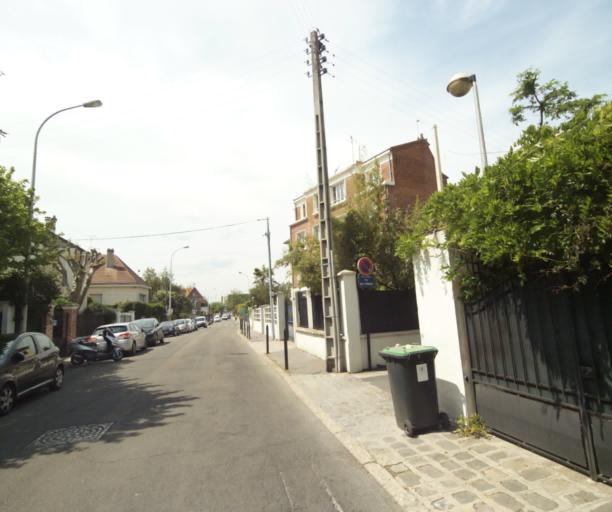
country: FR
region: Ile-de-France
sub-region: Departement des Hauts-de-Seine
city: Bois-Colombes
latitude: 48.9088
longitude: 2.2649
